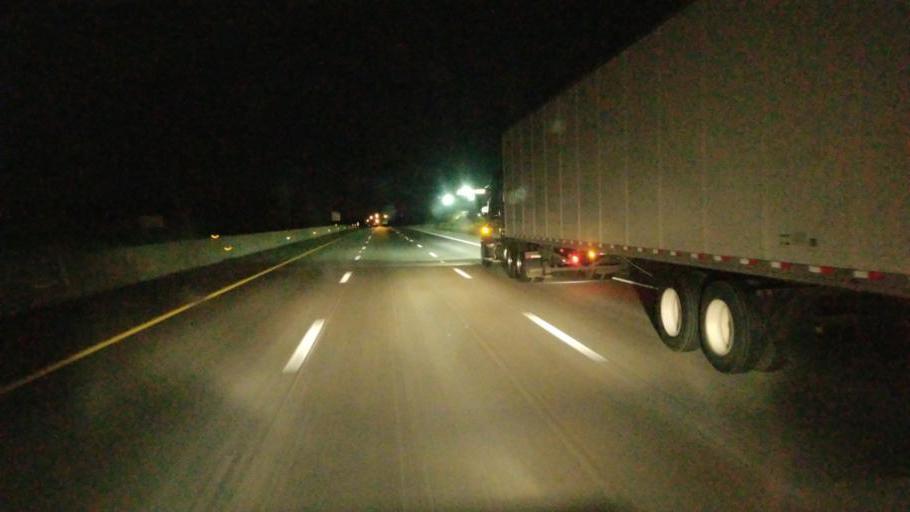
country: US
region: Ohio
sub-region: Clark County
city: Park Layne
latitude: 39.8659
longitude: -84.0670
